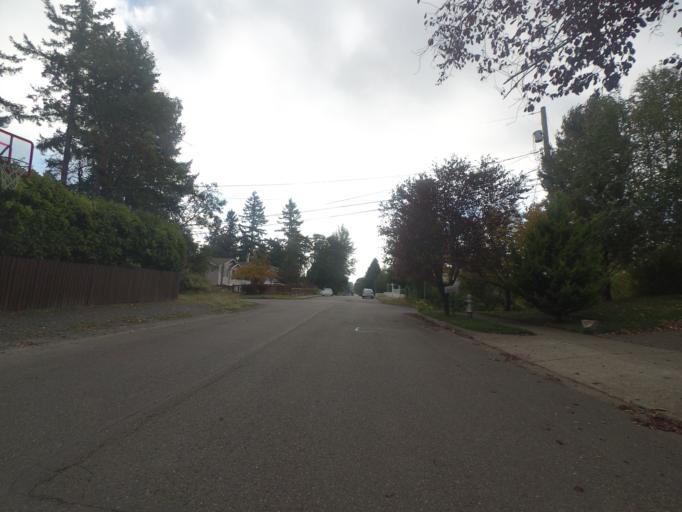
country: US
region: Washington
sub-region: Pierce County
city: Lakewood
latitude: 47.2015
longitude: -122.5021
